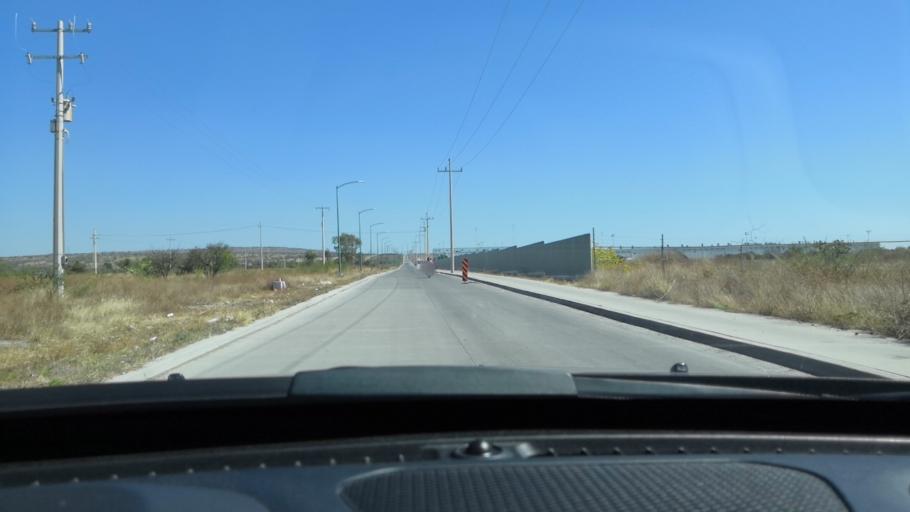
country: MX
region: Guanajuato
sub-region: Leon
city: Centro Familiar la Soledad
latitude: 21.1016
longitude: -101.7732
